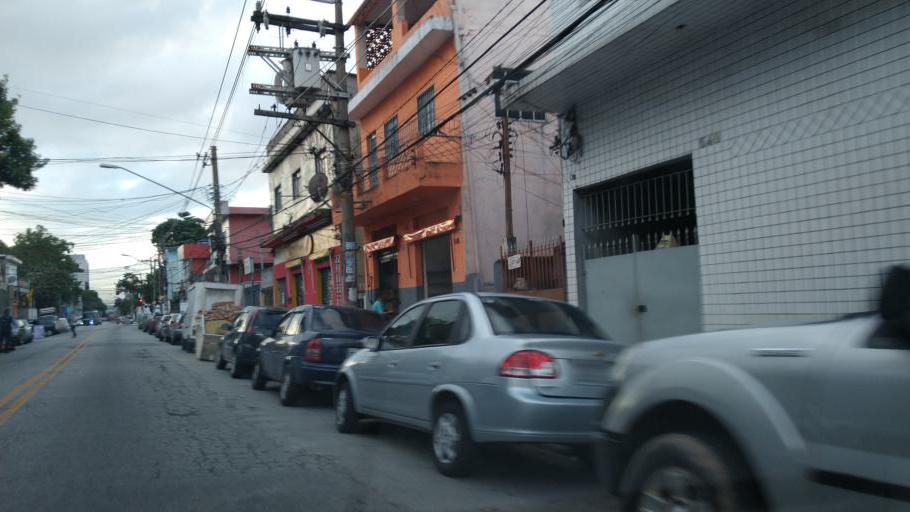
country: BR
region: Sao Paulo
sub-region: Guarulhos
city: Guarulhos
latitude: -23.4823
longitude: -46.5709
